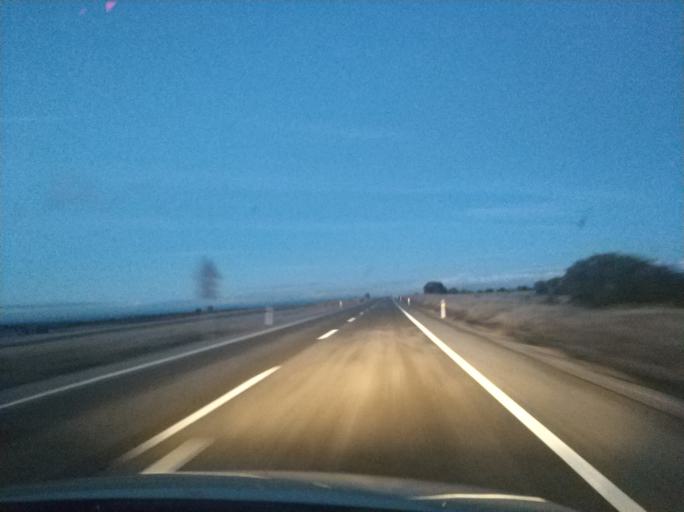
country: ES
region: Castille and Leon
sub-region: Provincia de Soria
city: Fuentecambron
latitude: 41.4789
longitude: -3.3193
